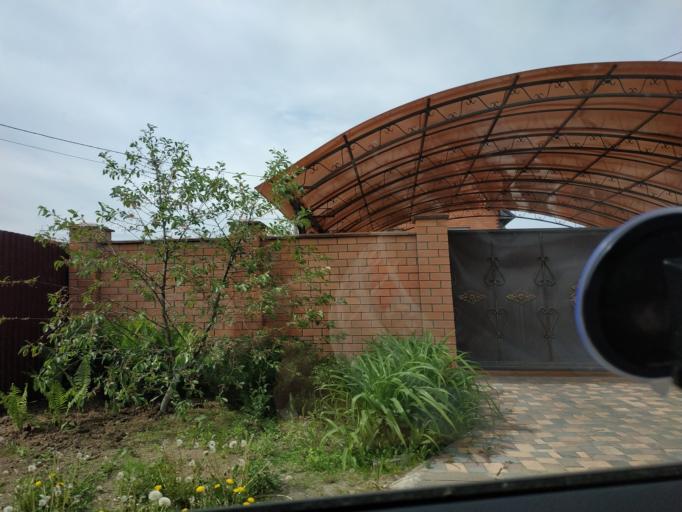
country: RU
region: Moskovskaya
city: Ramenskoye
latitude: 55.5526
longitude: 38.2882
